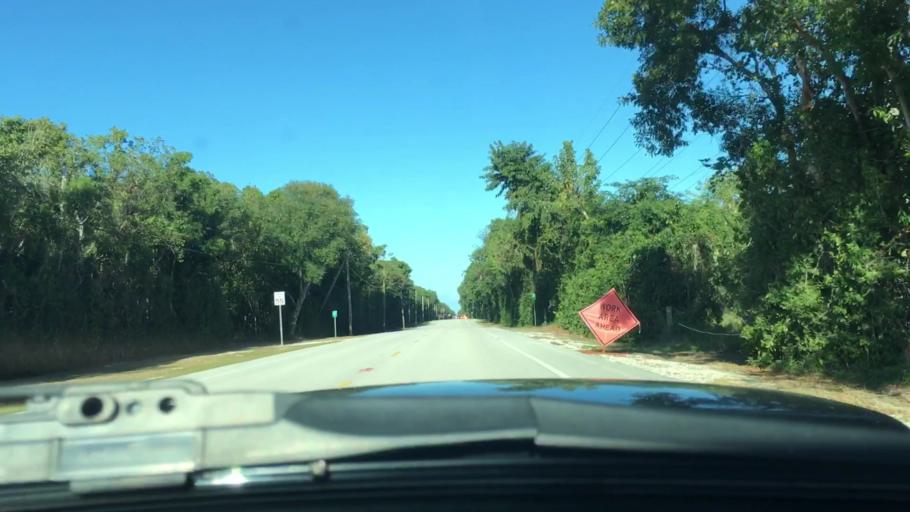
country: US
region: Florida
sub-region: Monroe County
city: North Key Largo
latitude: 25.1811
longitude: -80.3653
